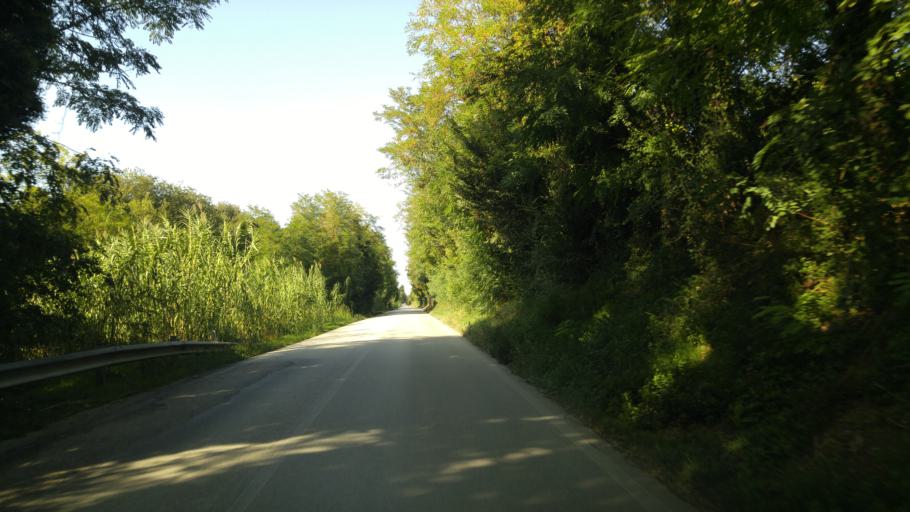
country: IT
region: The Marches
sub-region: Provincia di Pesaro e Urbino
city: Bellocchi
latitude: 43.8033
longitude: 13.0205
